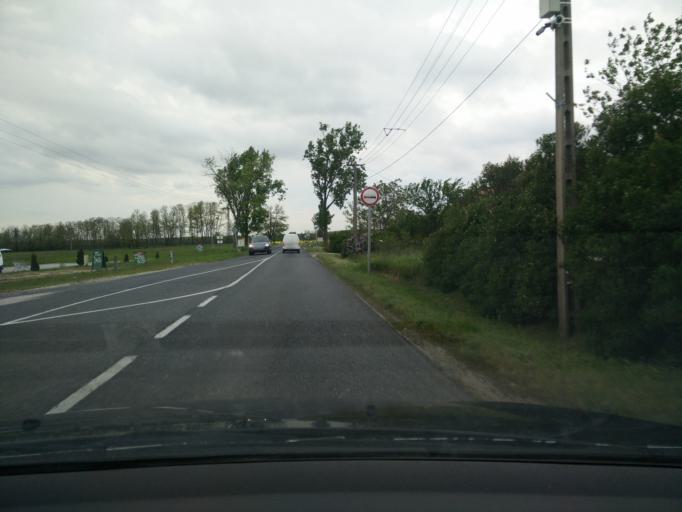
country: HU
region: Gyor-Moson-Sopron
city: Tet
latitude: 47.5236
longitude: 17.5188
